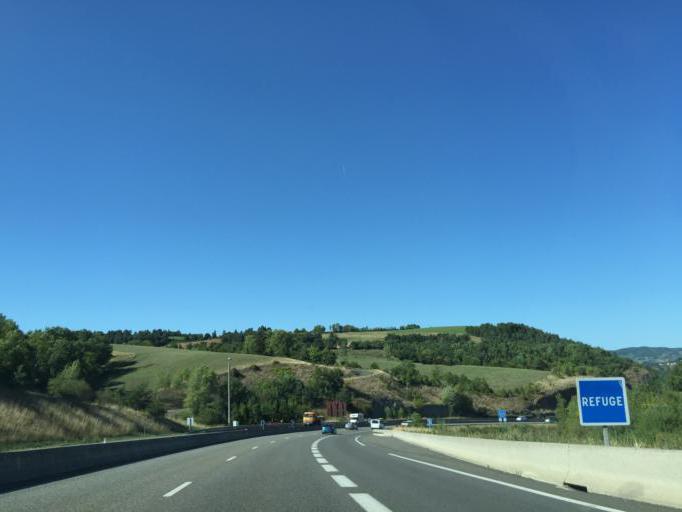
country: FR
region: Languedoc-Roussillon
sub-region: Departement de la Lozere
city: La Canourgue
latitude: 44.4217
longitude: 3.1840
